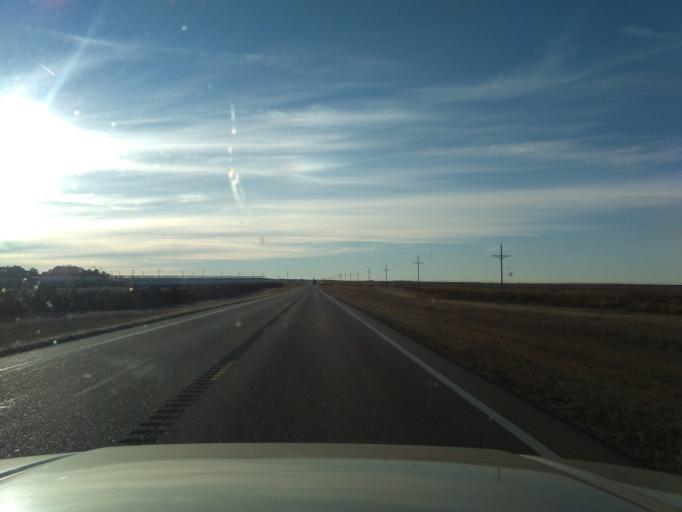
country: US
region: Kansas
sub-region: Thomas County
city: Colby
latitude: 39.4470
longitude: -100.8243
